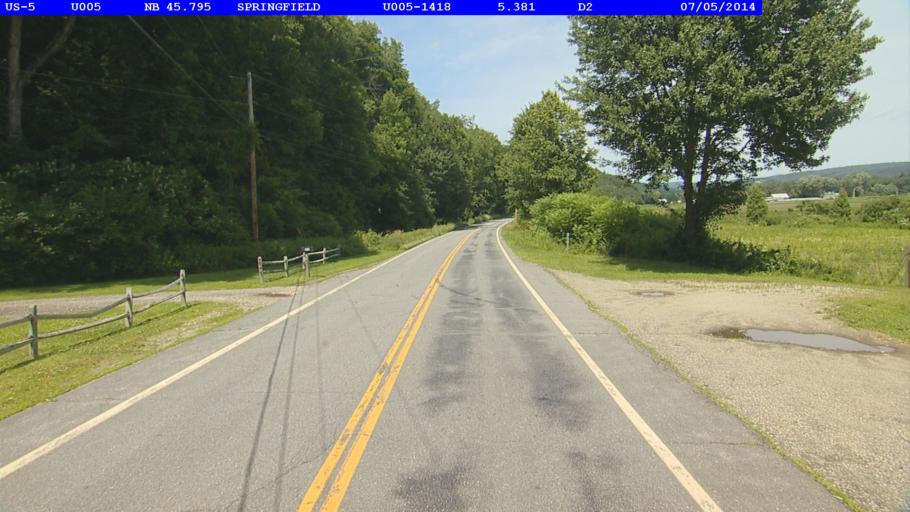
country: US
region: New Hampshire
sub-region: Sullivan County
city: Charlestown
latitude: 43.2913
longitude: -72.4127
